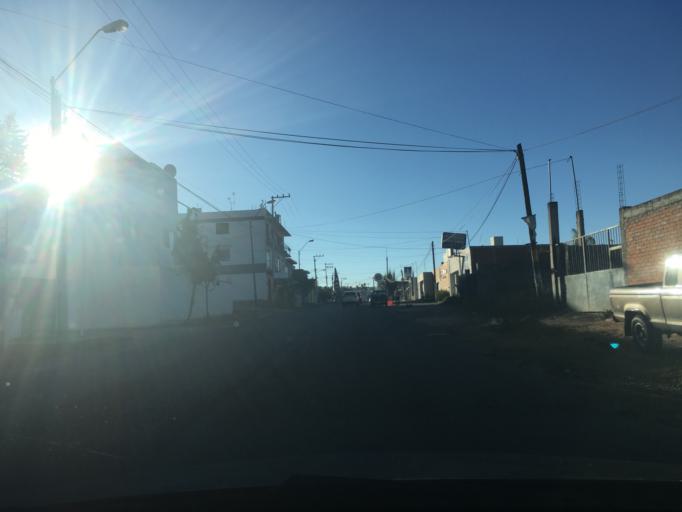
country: MX
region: Michoacan
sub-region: Morelia
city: Montana Monarca (Punta Altozano)
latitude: 19.6607
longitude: -101.1589
